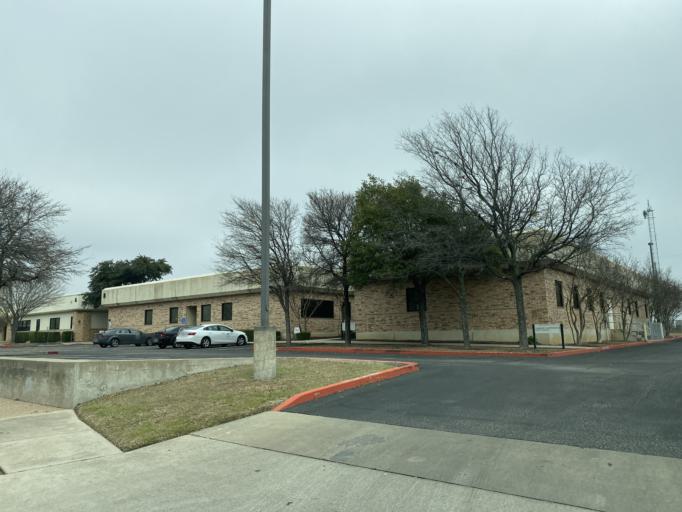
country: US
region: Texas
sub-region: Williamson County
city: Round Rock
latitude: 30.5311
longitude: -97.6853
